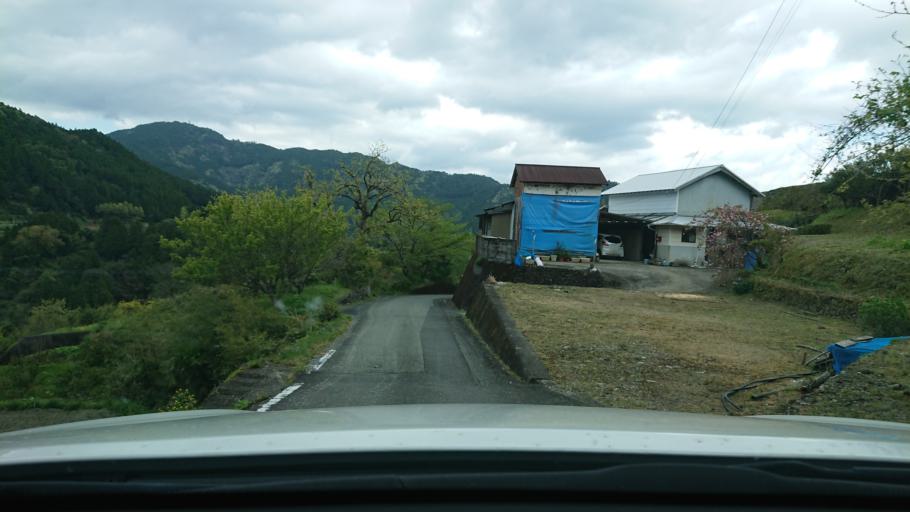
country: JP
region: Tokushima
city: Kamojimacho-jogejima
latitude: 33.8856
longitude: 134.3934
